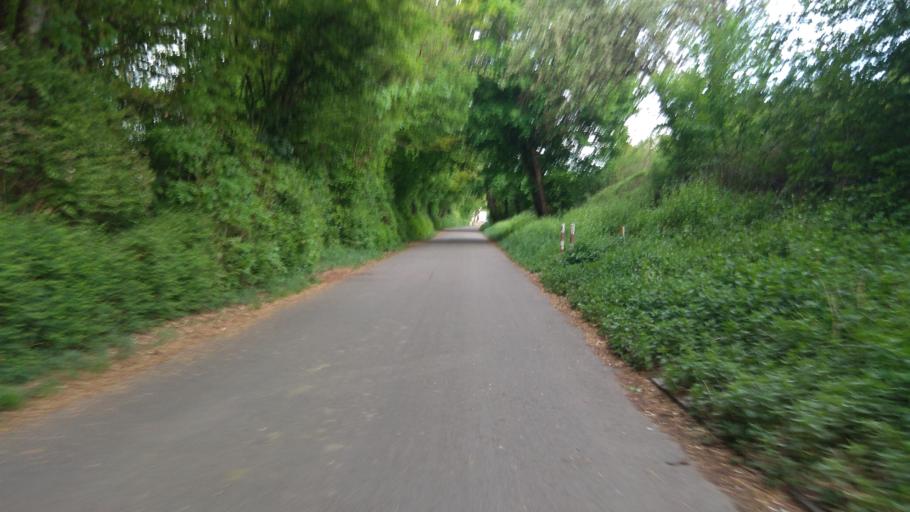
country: DE
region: Baden-Wuerttemberg
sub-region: Tuebingen Region
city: Wannweil
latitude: 48.5006
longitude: 9.1677
